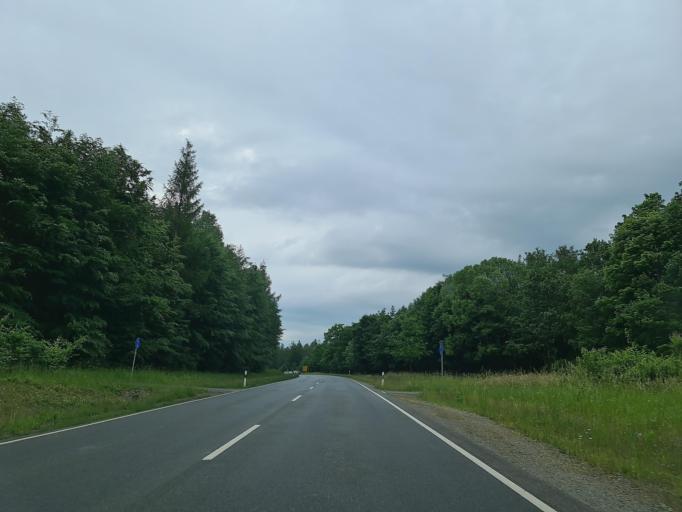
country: DE
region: Saxony
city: Lengenfeld
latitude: 50.5439
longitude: 12.3418
